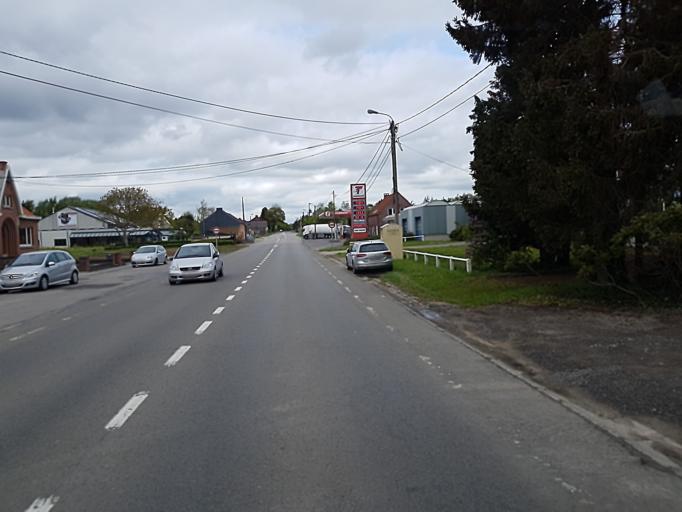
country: BE
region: Wallonia
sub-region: Province du Brabant Wallon
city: Jodoigne
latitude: 50.7420
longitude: 4.8798
